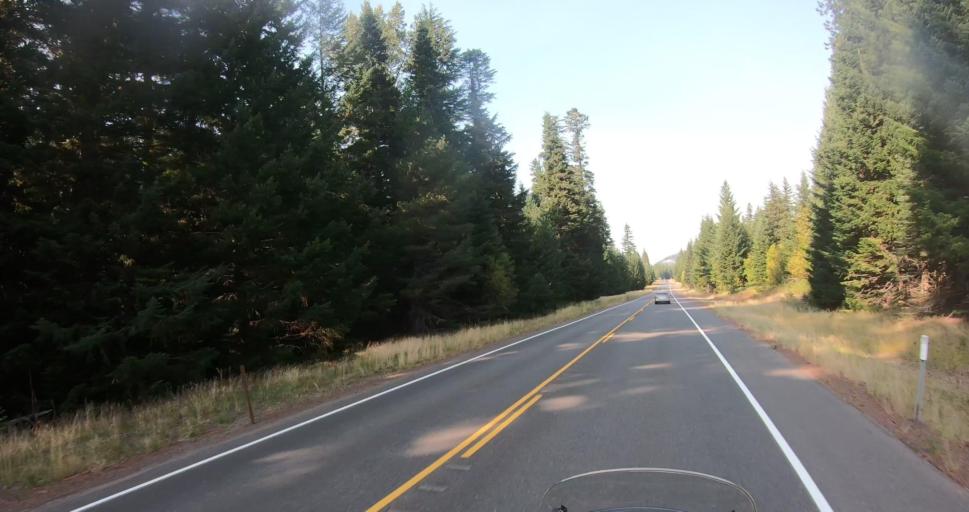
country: US
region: Oregon
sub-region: Hood River County
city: Odell
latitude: 45.3591
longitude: -121.5681
